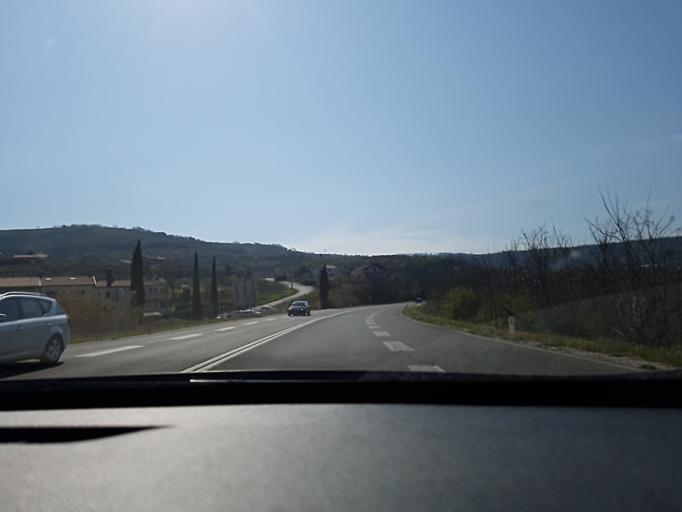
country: SI
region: Izola-Isola
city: Izola
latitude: 45.5394
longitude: 13.6761
